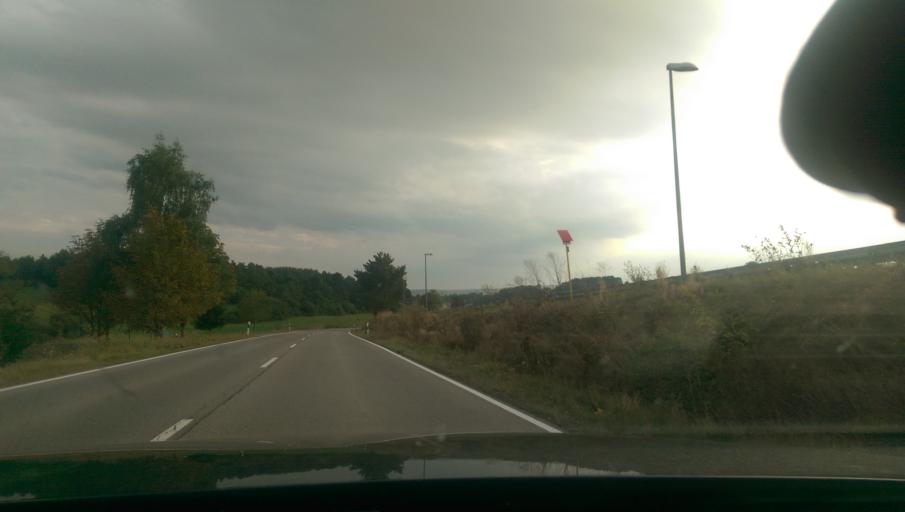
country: DE
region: Baden-Wuerttemberg
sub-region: Karlsruhe Region
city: Heimsheim
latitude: 48.8225
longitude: 8.8672
